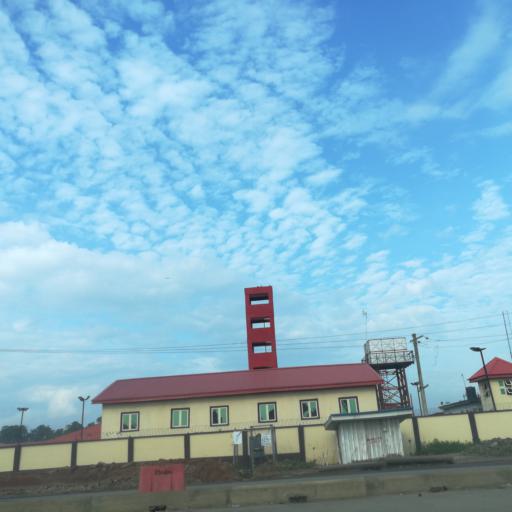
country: NG
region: Lagos
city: Oshodi
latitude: 6.5651
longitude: 3.3480
